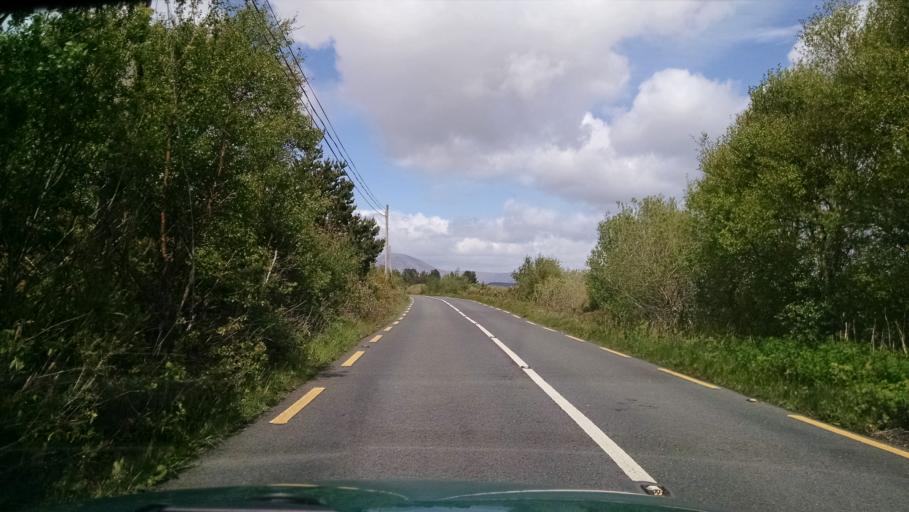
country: IE
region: Connaught
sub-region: County Galway
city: Oughterard
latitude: 53.3710
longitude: -9.5435
